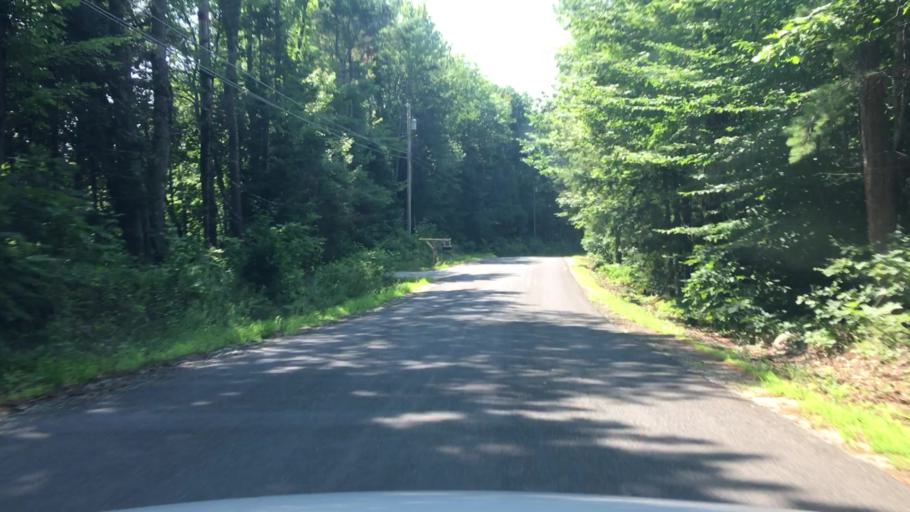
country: US
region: Maine
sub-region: Androscoggin County
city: Greene
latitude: 44.2228
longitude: -70.1045
